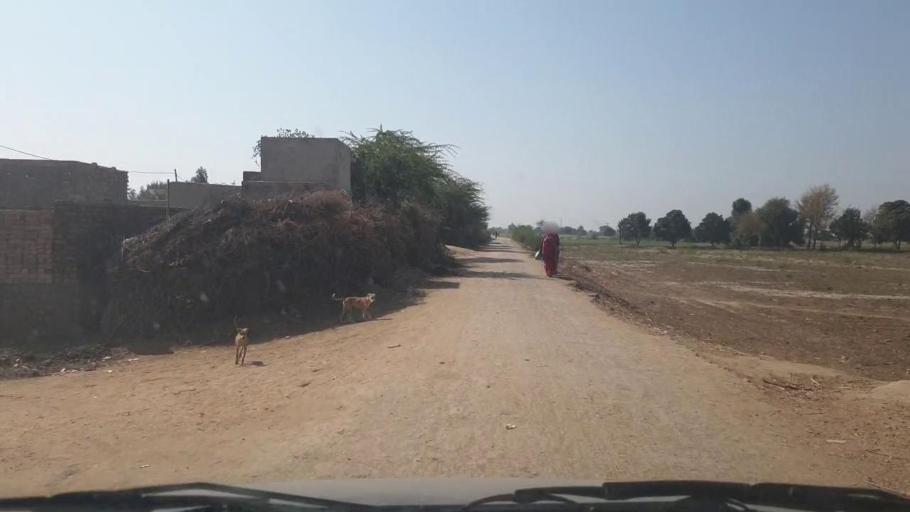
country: PK
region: Sindh
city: Samaro
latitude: 25.2810
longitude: 69.2948
